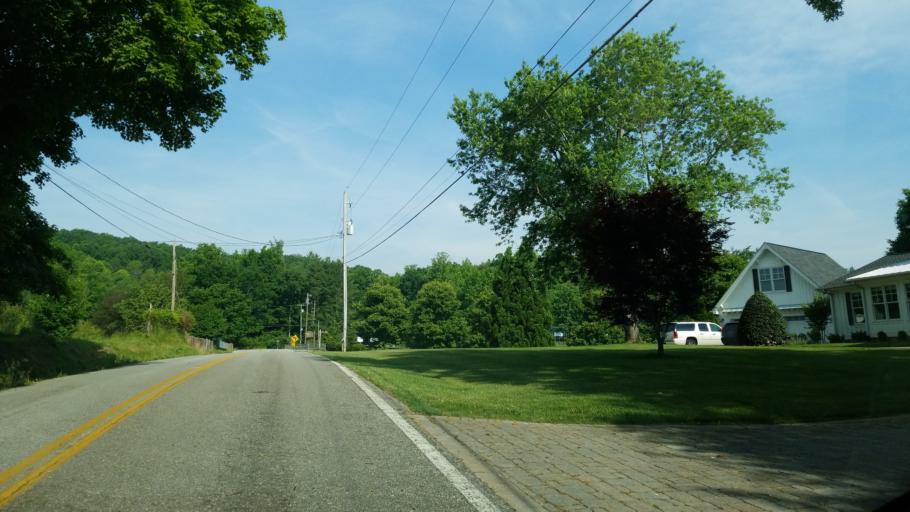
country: US
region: Tennessee
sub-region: Hamilton County
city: Collegedale
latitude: 35.0997
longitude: -85.0180
